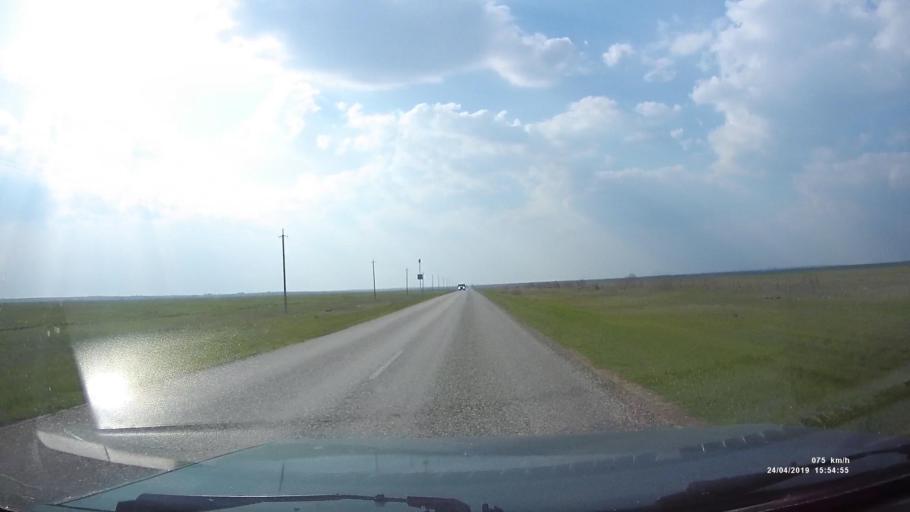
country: RU
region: Kalmykiya
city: Yashalta
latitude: 46.5870
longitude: 42.5591
